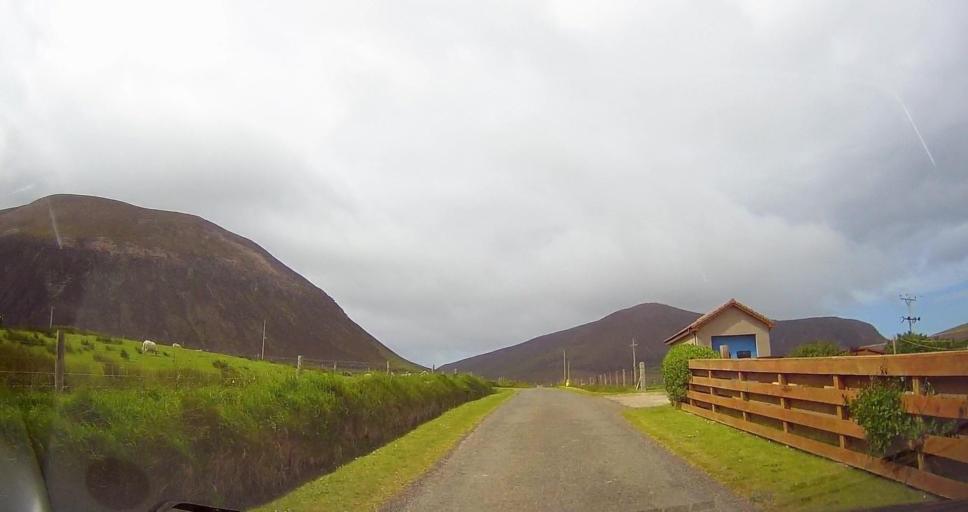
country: GB
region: Scotland
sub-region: Orkney Islands
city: Stromness
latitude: 58.9146
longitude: -3.3321
